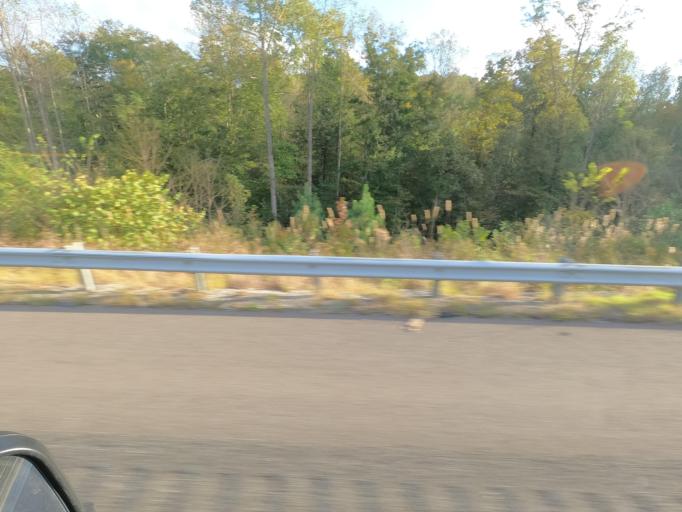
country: US
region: Tennessee
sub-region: Decatur County
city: Parsons
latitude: 35.8150
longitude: -88.2037
